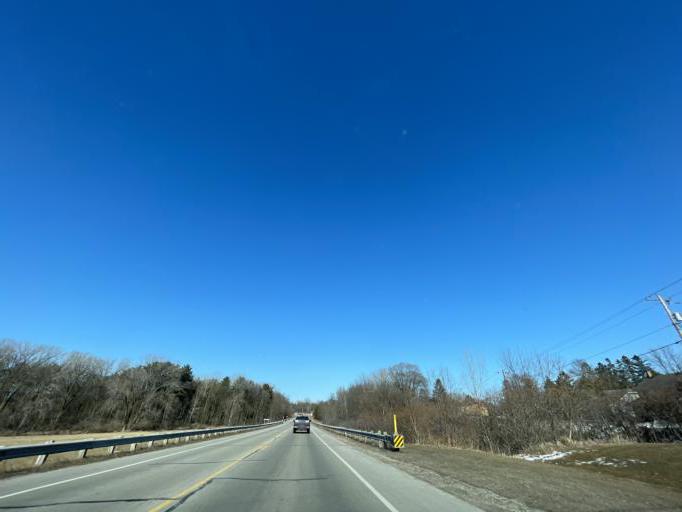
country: US
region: Wisconsin
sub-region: Brown County
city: Suamico
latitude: 44.6309
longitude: -88.0550
